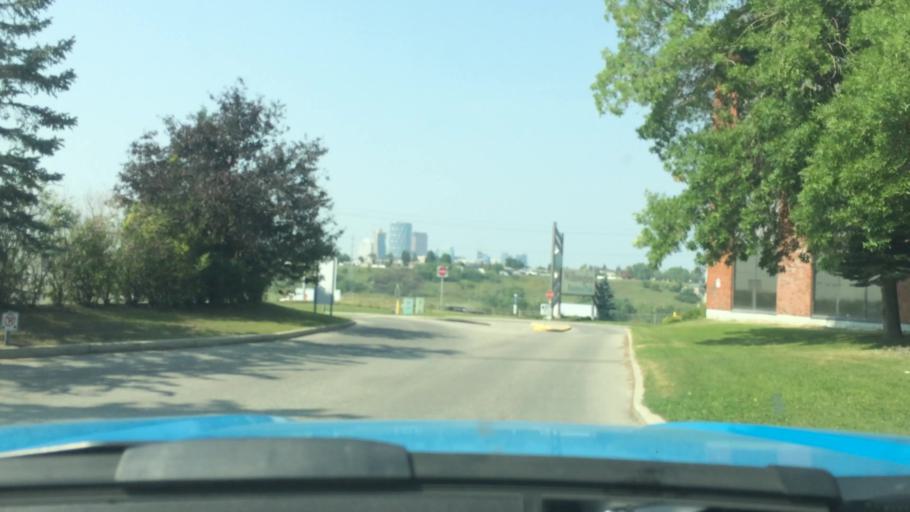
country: CA
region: Alberta
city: Calgary
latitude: 51.0562
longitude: -114.0190
